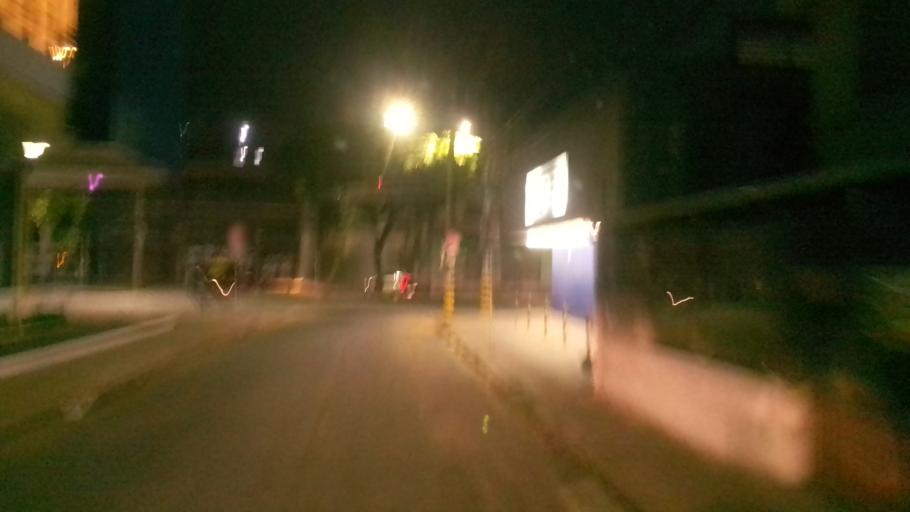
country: BR
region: Minas Gerais
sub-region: Belo Horizonte
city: Belo Horizonte
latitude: -19.9073
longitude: -43.9593
